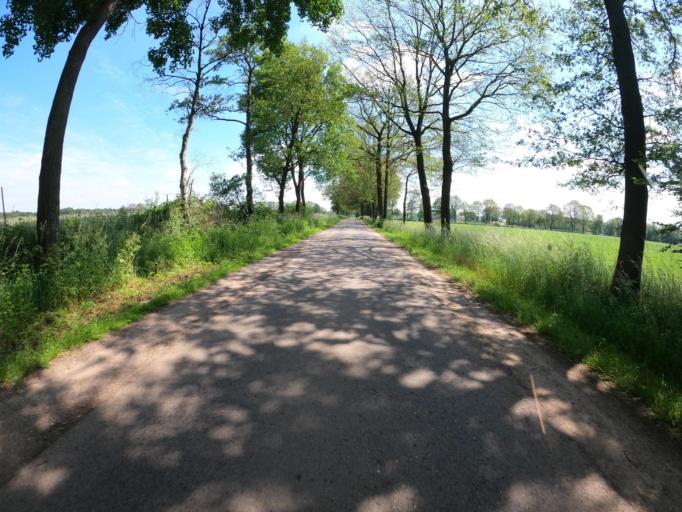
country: DE
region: North Rhine-Westphalia
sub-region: Regierungsbezirk Dusseldorf
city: Schermbeck
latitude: 51.6901
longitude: 6.8315
